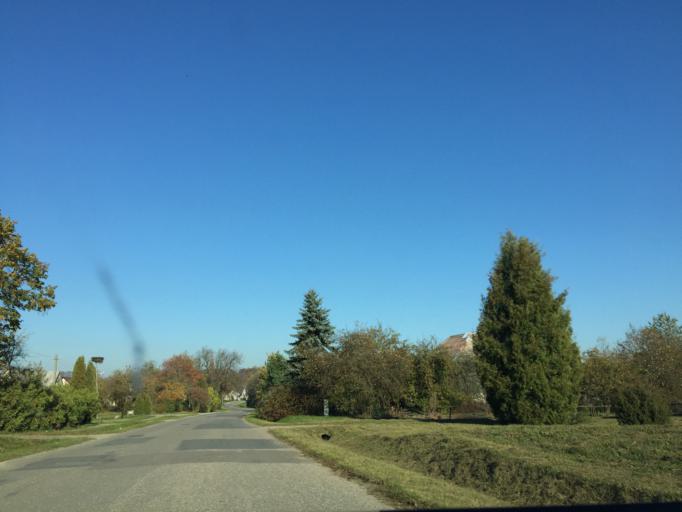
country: LT
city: Salantai
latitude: 55.9923
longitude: 21.6711
